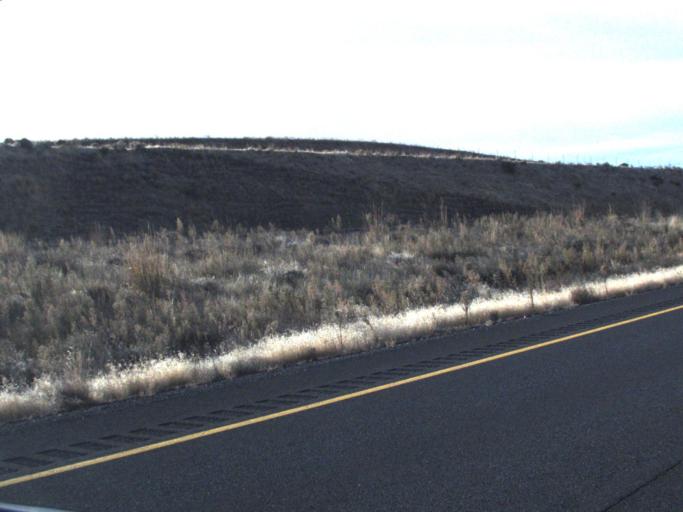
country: US
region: Washington
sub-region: Franklin County
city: Connell
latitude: 46.8584
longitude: -118.6354
